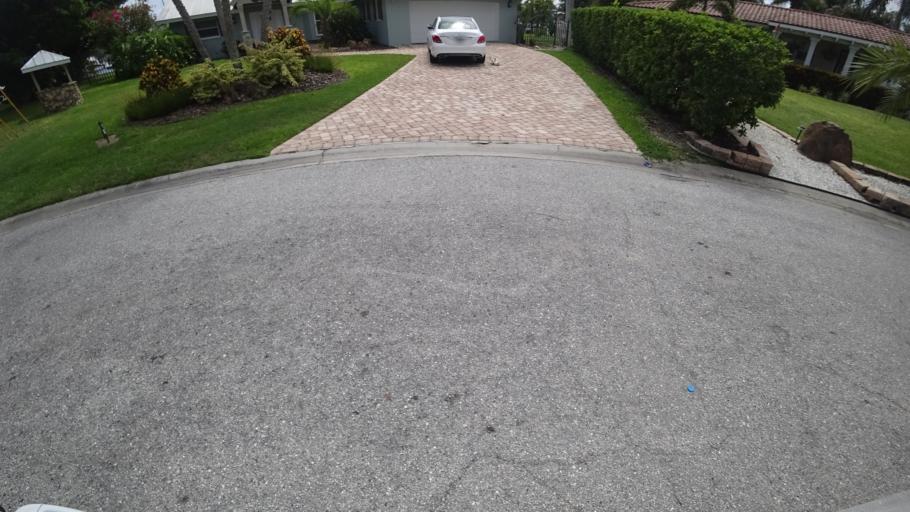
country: US
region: Florida
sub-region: Manatee County
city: Whitfield
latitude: 27.4132
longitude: -82.5755
